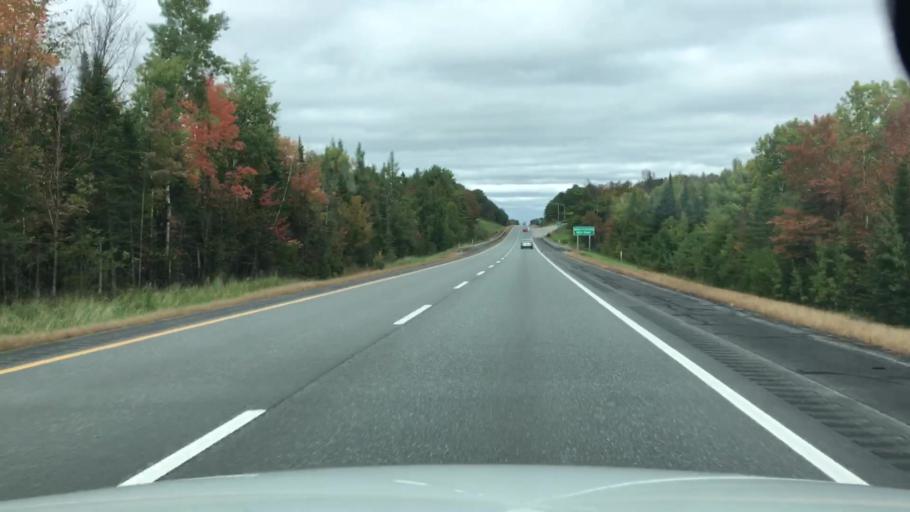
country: US
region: Maine
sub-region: Waldo County
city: Burnham
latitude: 44.7409
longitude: -69.4286
